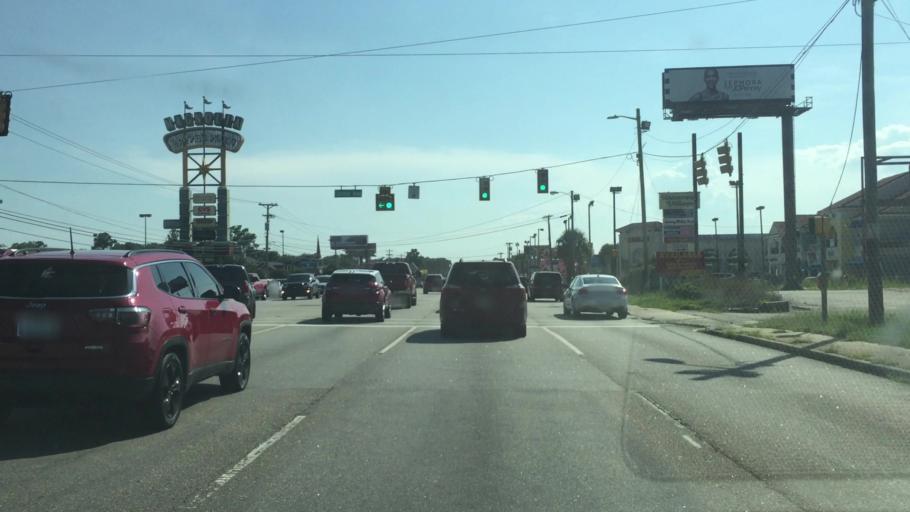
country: US
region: South Carolina
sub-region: Horry County
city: North Myrtle Beach
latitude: 33.7812
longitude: -78.7893
